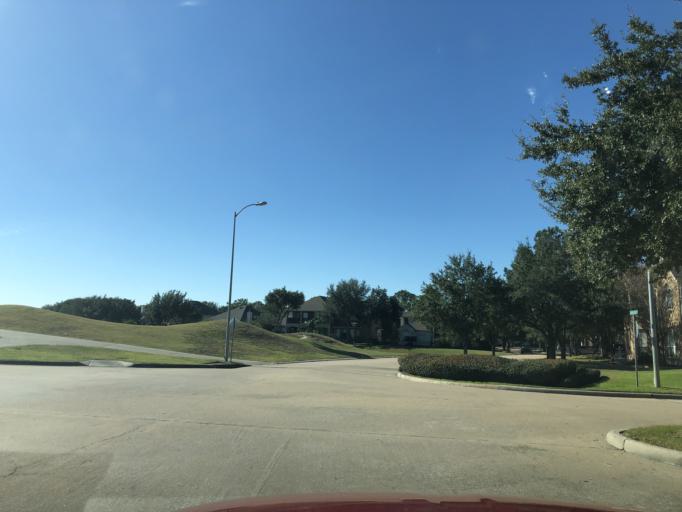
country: US
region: Texas
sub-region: Harris County
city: Oak Cliff Place
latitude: 29.9426
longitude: -95.6650
